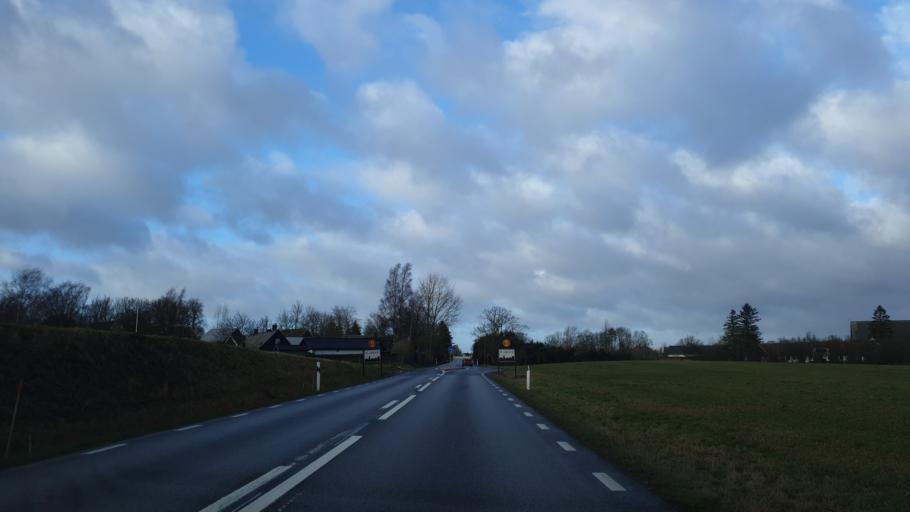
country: SE
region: Skane
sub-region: Malmo
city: Oxie
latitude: 55.4692
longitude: 13.1387
